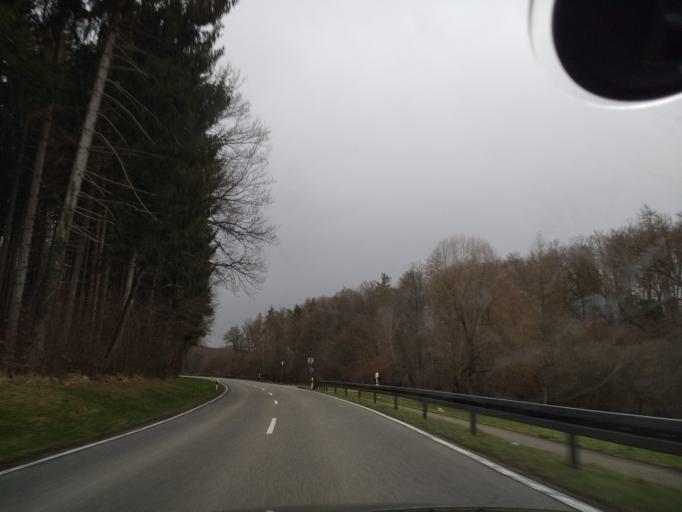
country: DE
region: Baden-Wuerttemberg
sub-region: Freiburg Region
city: Allensbach
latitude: 47.7241
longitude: 9.1290
